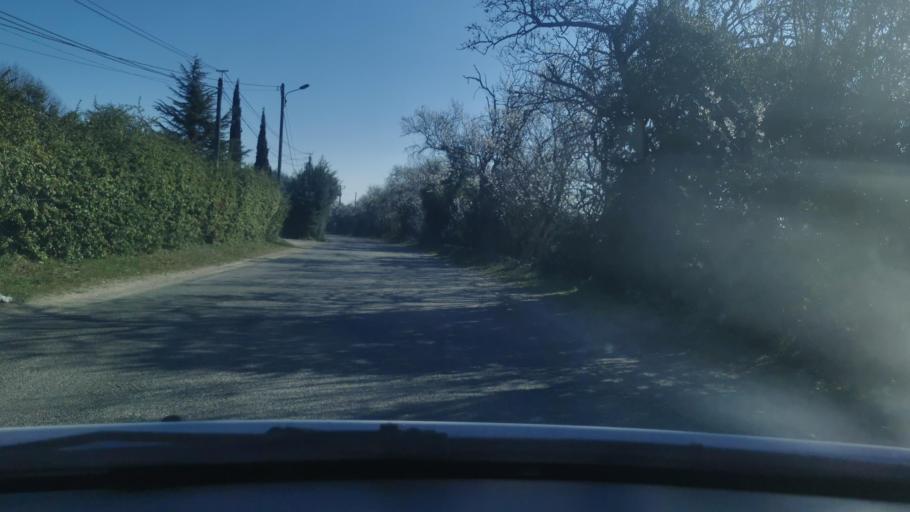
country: FR
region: Languedoc-Roussillon
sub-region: Departement du Gard
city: Montaren-et-Saint-Mediers
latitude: 44.0454
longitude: 4.4010
